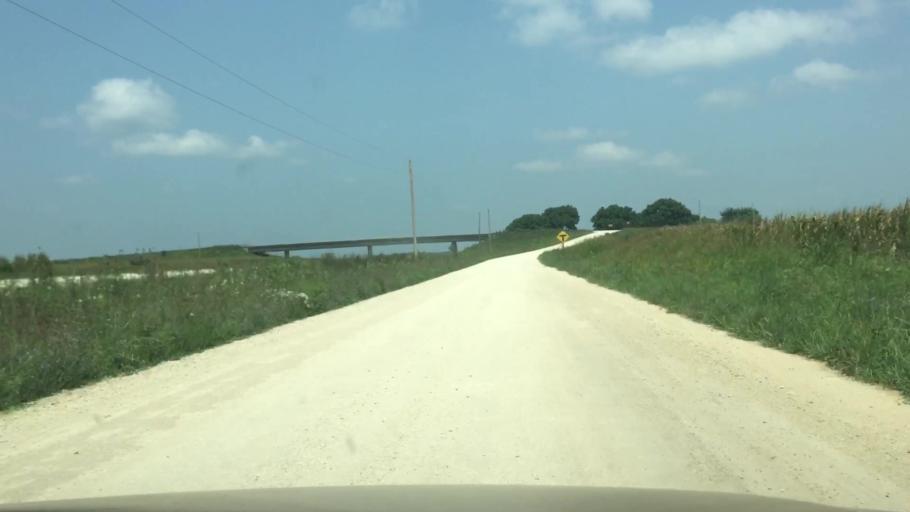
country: US
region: Kansas
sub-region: Allen County
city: Humboldt
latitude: 37.8466
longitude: -95.4094
